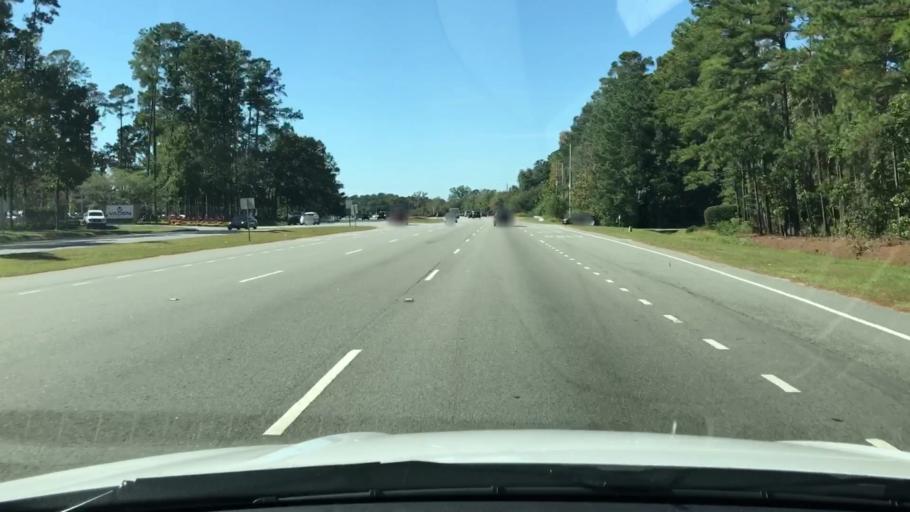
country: US
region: South Carolina
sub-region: Beaufort County
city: Bluffton
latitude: 32.2911
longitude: -80.9136
